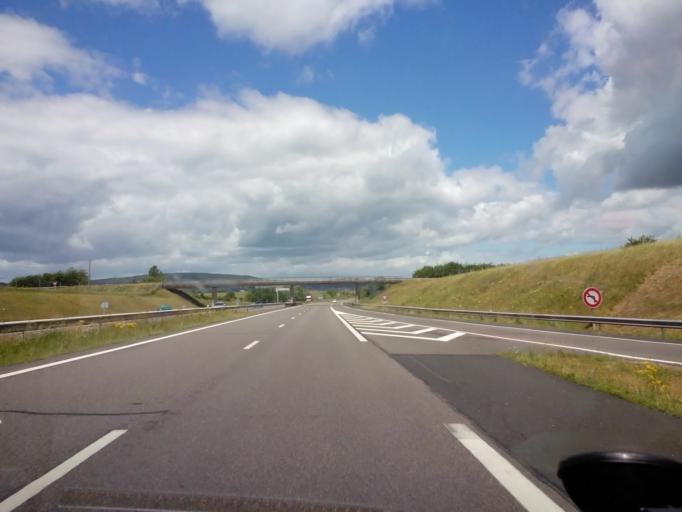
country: FR
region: Lorraine
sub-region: Departement des Vosges
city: Chatenois
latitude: 48.2710
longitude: 5.8600
